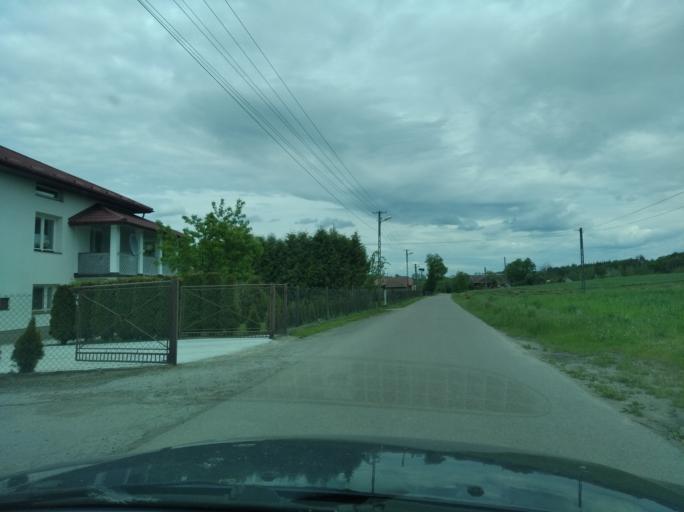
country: PL
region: Subcarpathian Voivodeship
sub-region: Powiat przeworski
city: Jawornik Polski
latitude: 49.8357
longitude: 22.3023
